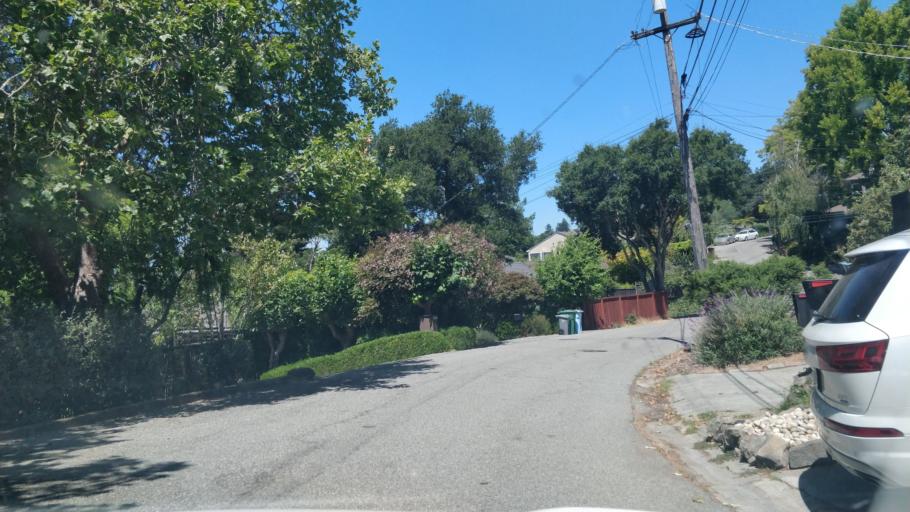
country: US
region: California
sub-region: Alameda County
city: Berkeley
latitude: 37.8862
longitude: -122.2538
